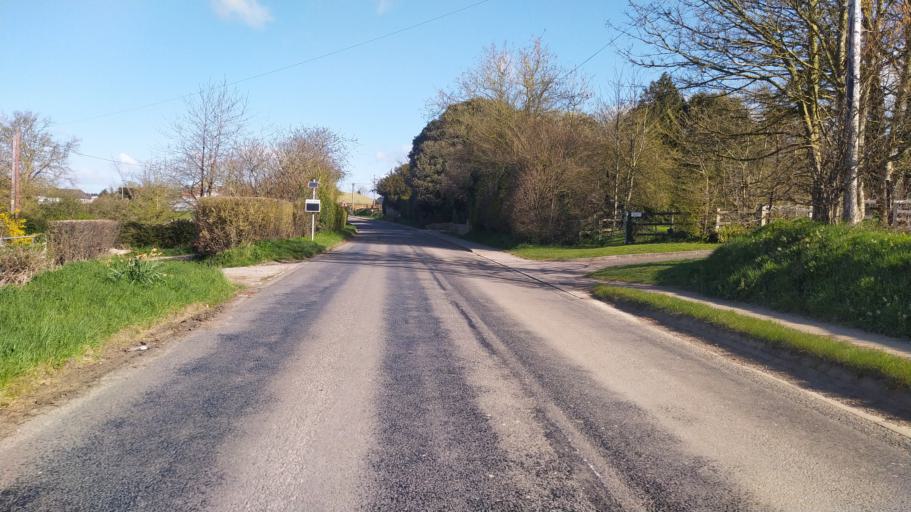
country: GB
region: England
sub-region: Dorset
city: Sturminster Newton
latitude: 50.9419
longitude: -2.3070
